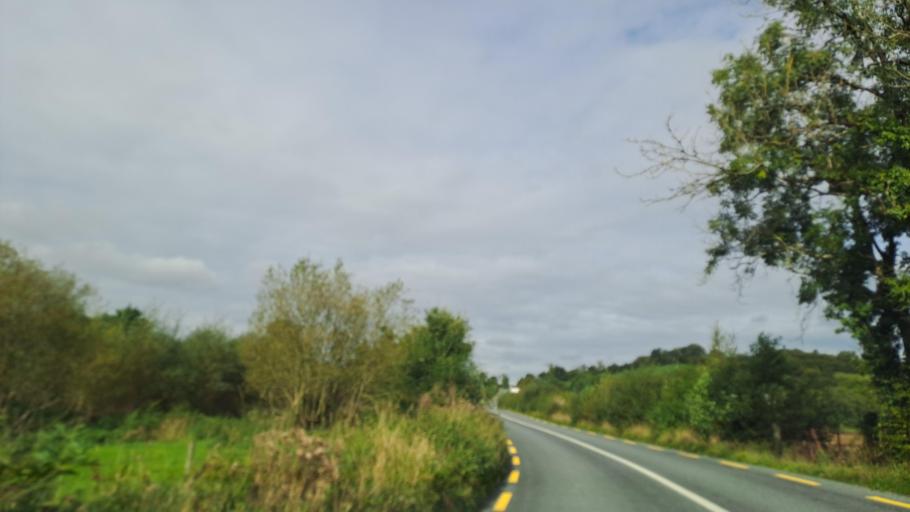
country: IE
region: Ulster
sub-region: An Cabhan
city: Kingscourt
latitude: 53.9708
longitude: -6.8667
